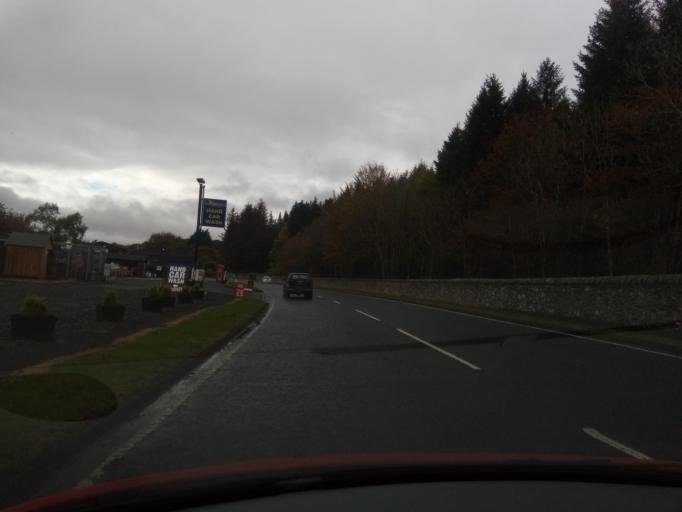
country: GB
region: Scotland
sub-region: The Scottish Borders
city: Galashiels
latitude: 55.6301
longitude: -2.8432
